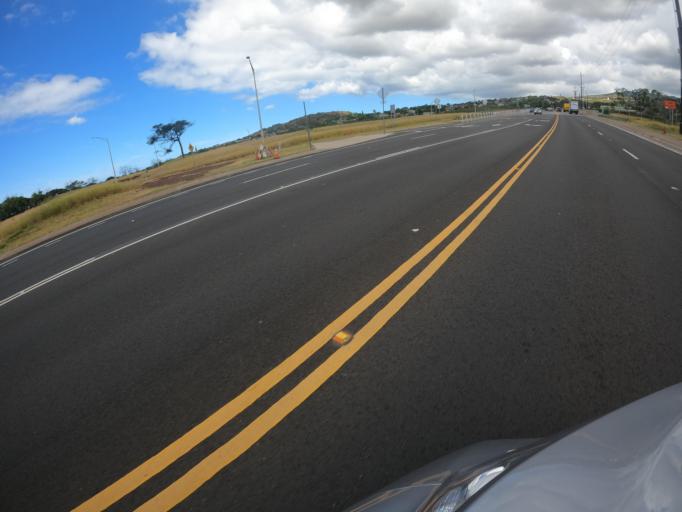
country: US
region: Hawaii
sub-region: Honolulu County
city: Makakilo City
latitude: 21.3406
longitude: -158.0768
